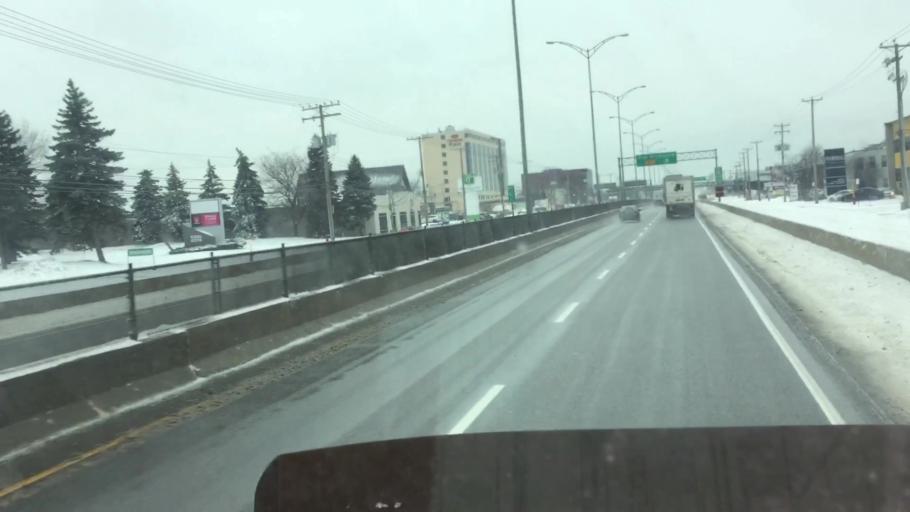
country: CA
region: Quebec
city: Saint-Laurent
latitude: 45.4870
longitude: -73.6900
